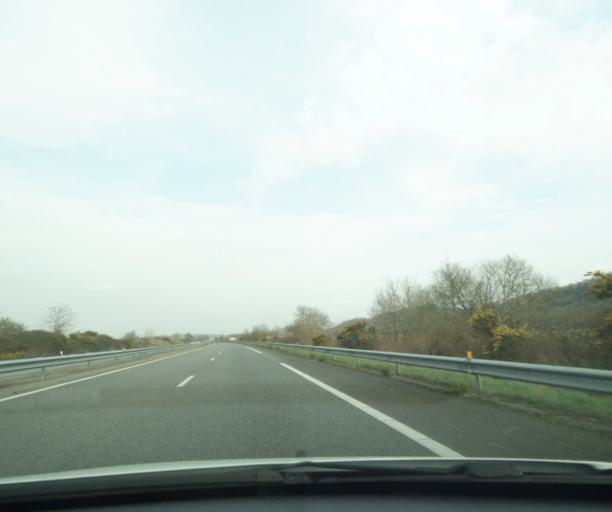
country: FR
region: Aquitaine
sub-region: Departement des Landes
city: Labatut
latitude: 43.5191
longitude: -0.9574
